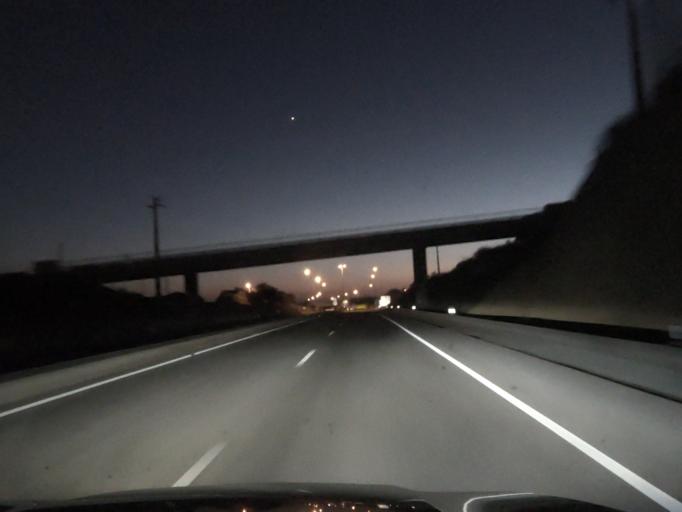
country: PT
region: Faro
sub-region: Loule
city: Loule
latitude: 37.1464
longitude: -8.0170
